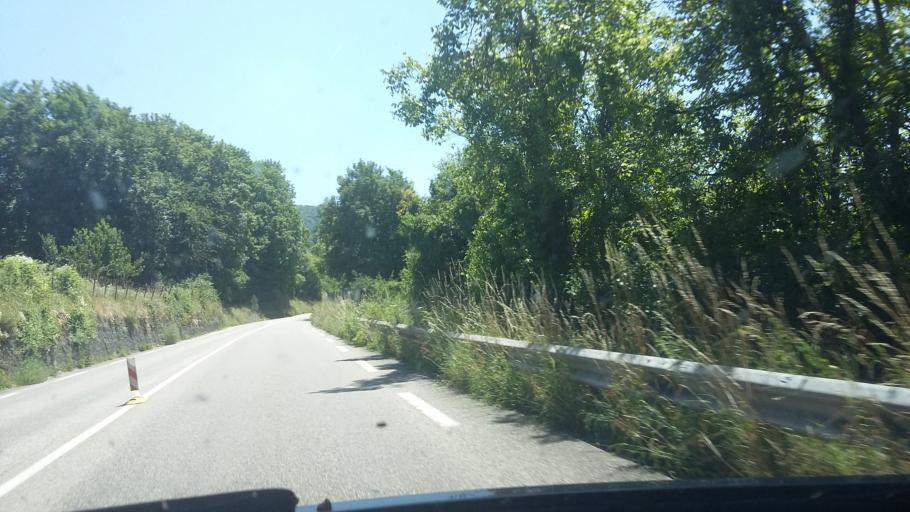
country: FR
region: Rhone-Alpes
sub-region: Departement de la Savoie
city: Yenne
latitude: 45.7137
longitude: 5.7143
